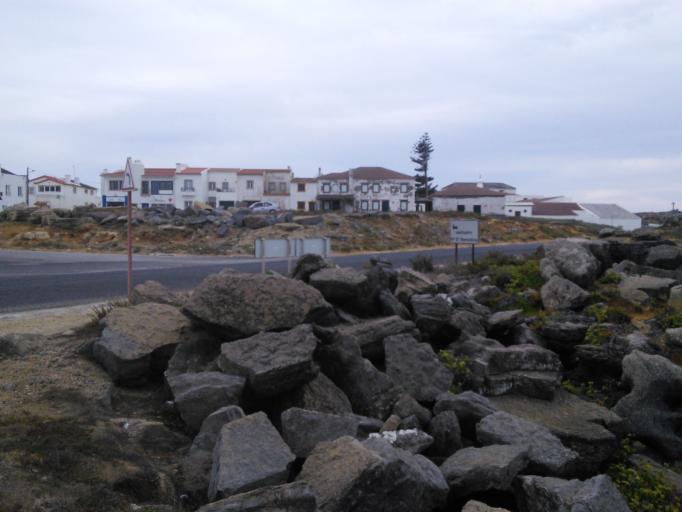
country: PT
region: Leiria
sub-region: Peniche
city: Peniche
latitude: 39.3673
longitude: -9.4022
